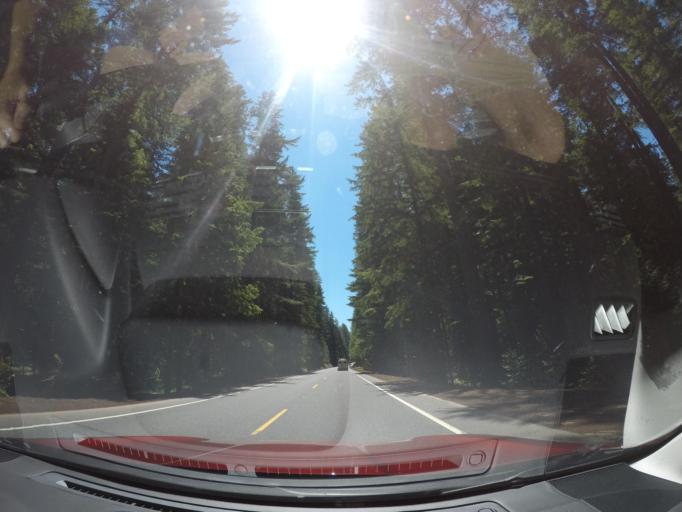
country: US
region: Oregon
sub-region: Linn County
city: Mill City
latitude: 44.6771
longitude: -121.9636
